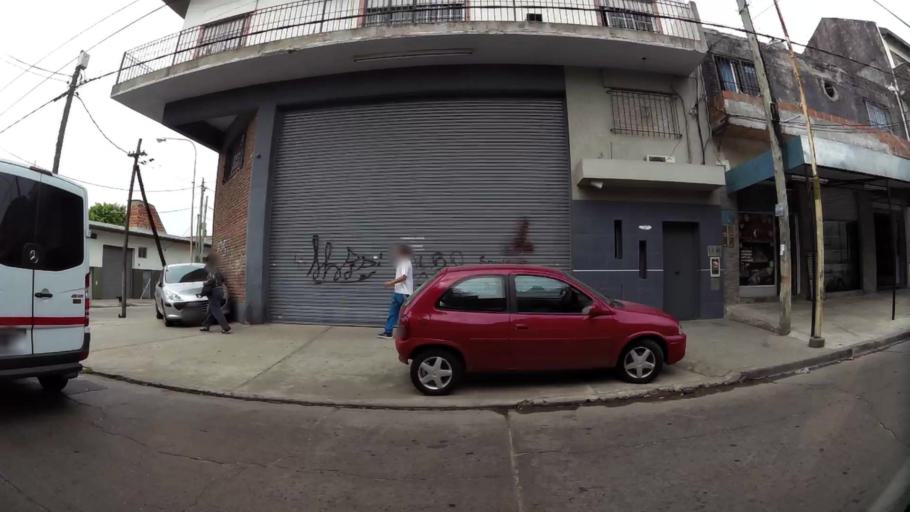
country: AR
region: Buenos Aires
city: San Justo
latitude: -34.6952
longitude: -58.5323
